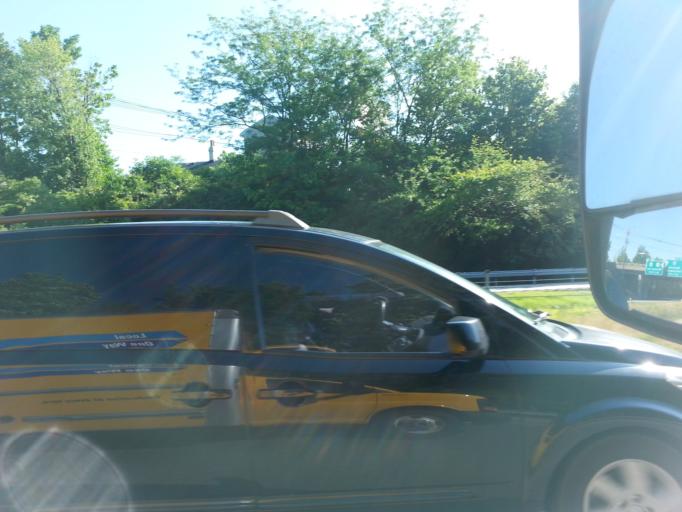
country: US
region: Indiana
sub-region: Clark County
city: Jeffersonville
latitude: 38.2519
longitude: -85.7174
